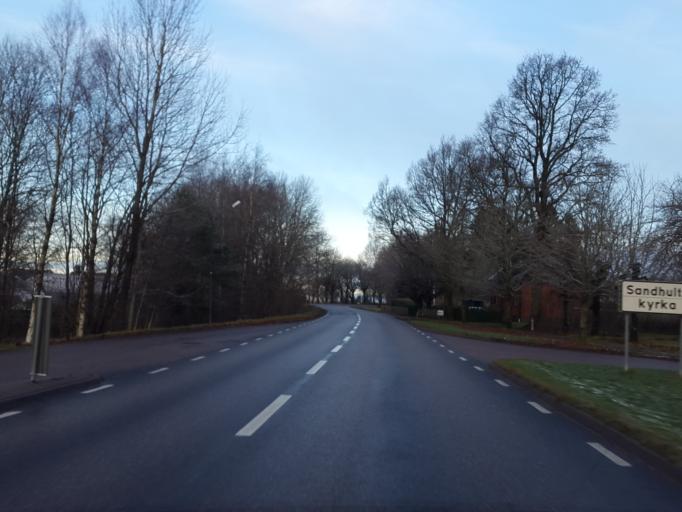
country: SE
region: Vaestra Goetaland
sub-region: Boras Kommun
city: Sjomarken
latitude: 57.7700
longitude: 12.8202
